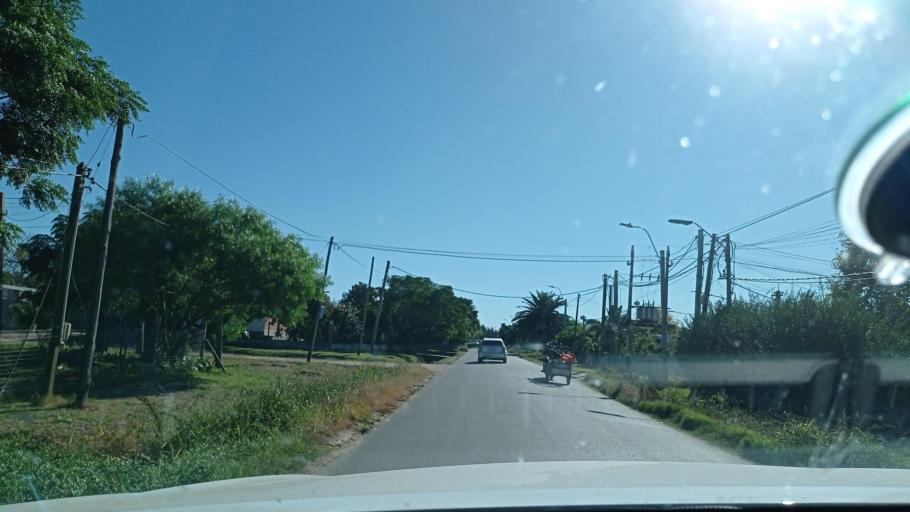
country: UY
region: Canelones
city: Joaquin Suarez
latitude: -34.7549
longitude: -55.9975
